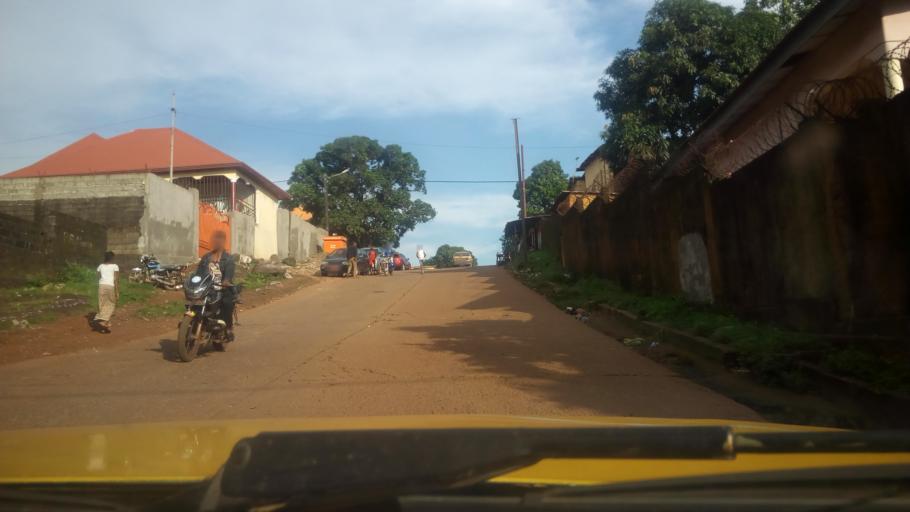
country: GN
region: Conakry
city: Conakry
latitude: 9.6218
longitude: -13.6101
